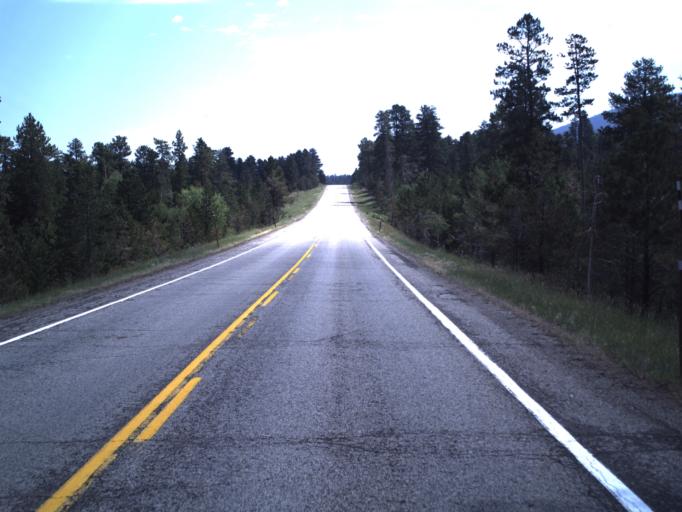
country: US
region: Utah
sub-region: Daggett County
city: Manila
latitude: 40.8509
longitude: -109.5789
